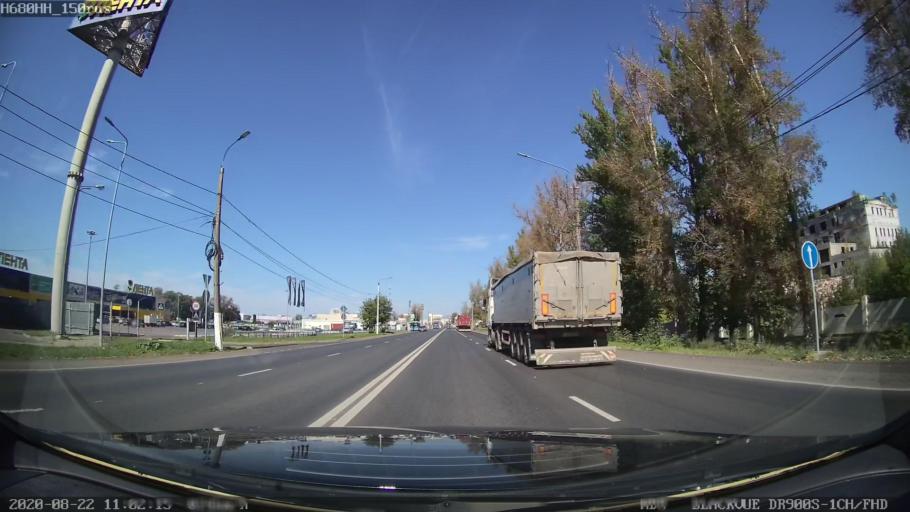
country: RU
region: Tverskaya
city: Tver
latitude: 56.8434
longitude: 35.9512
